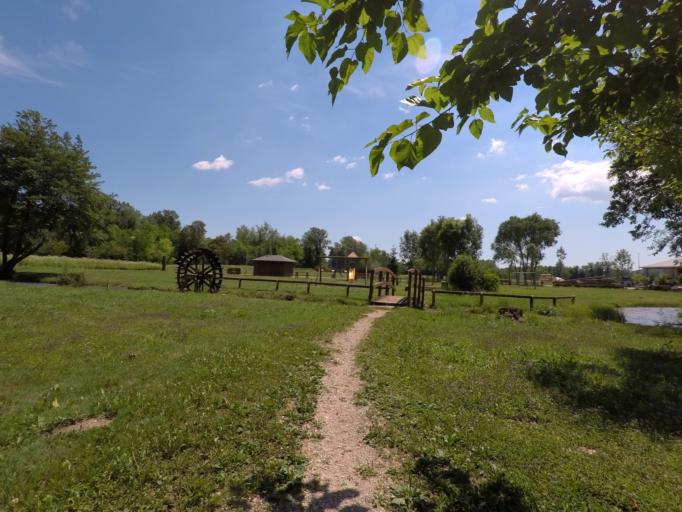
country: IT
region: Friuli Venezia Giulia
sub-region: Provincia di Udine
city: Forgaria nel Friuli
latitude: 46.2257
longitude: 13.0200
